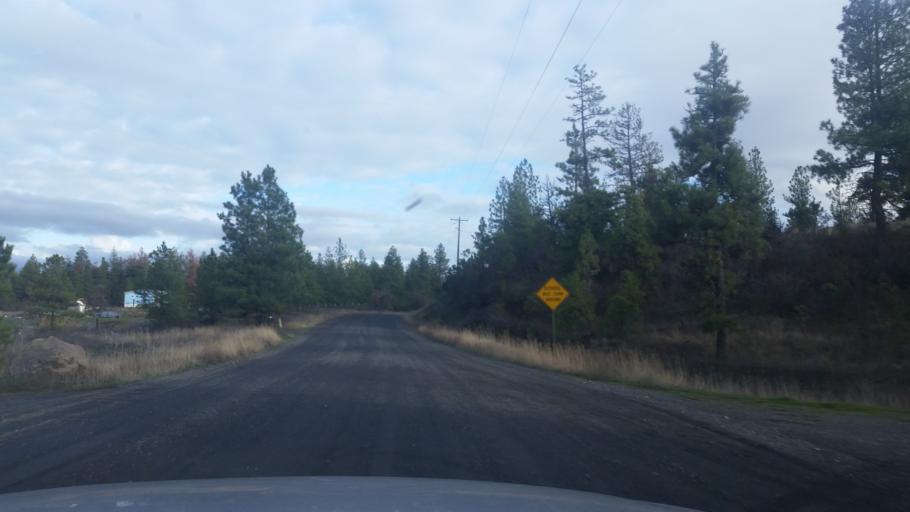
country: US
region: Washington
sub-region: Spokane County
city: Cheney
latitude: 47.4346
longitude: -117.4588
